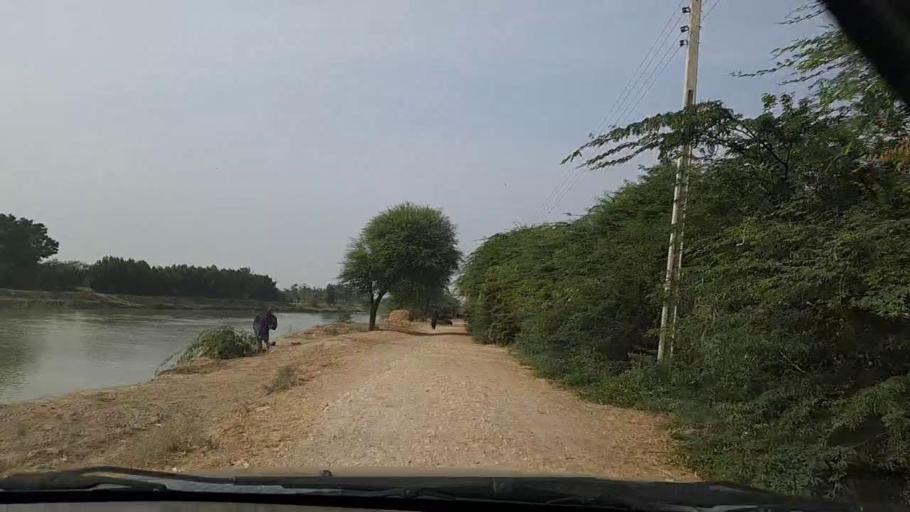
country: PK
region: Sindh
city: Thatta
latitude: 24.5708
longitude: 67.8565
